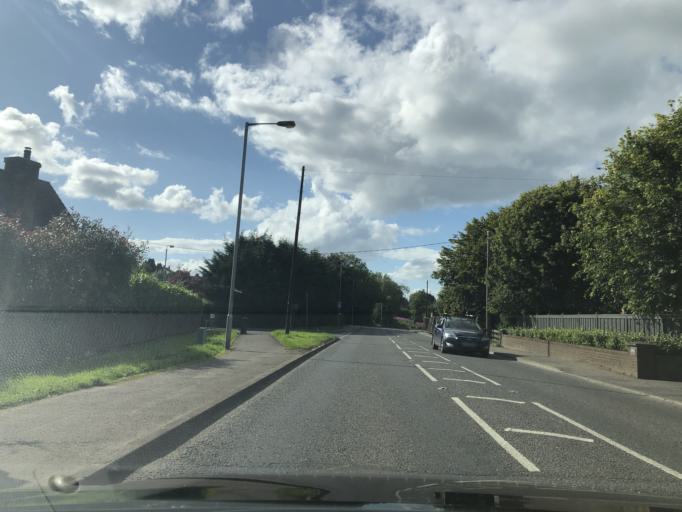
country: GB
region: Northern Ireland
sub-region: Castlereagh District
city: Dundonald
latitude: 54.5834
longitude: -5.7965
